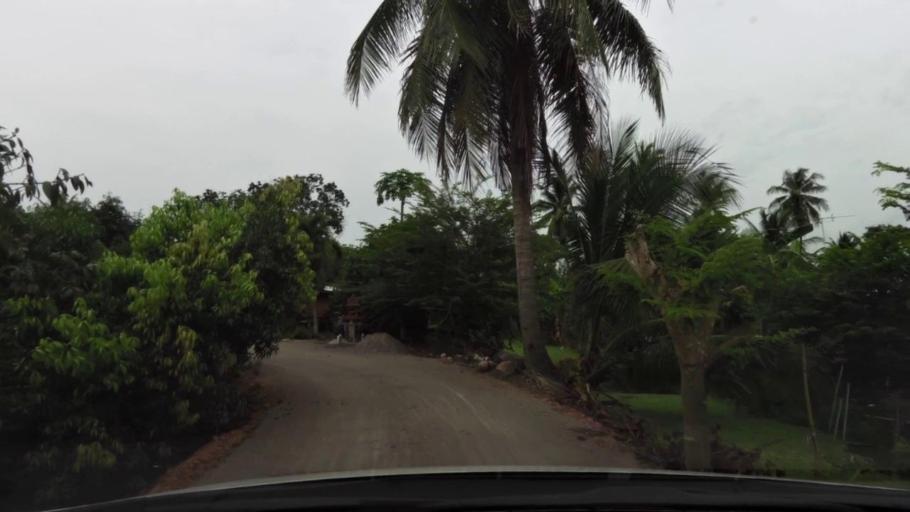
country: TH
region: Samut Sakhon
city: Ban Phaeo
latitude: 13.5893
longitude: 100.0328
